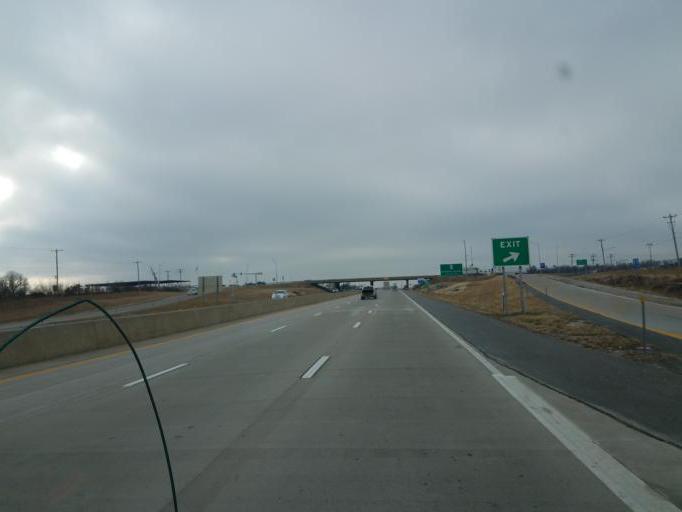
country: US
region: Missouri
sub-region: Greene County
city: Springfield
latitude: 37.2267
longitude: -93.2253
